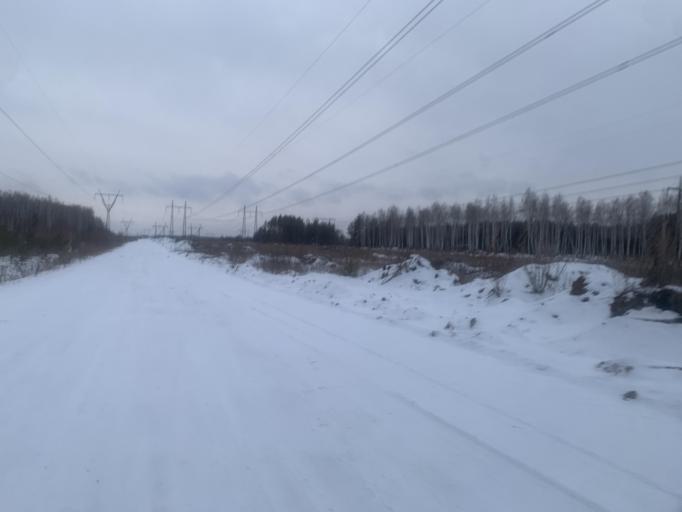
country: RU
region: Chelyabinsk
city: Roshchino
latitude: 55.1981
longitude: 61.2618
